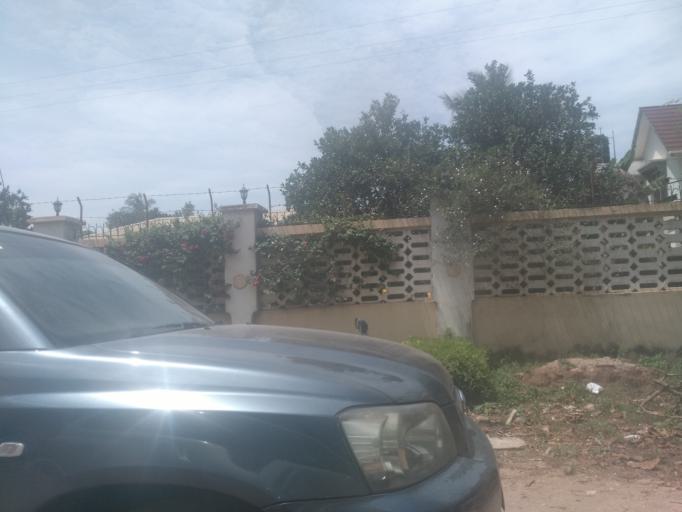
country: TZ
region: Zanzibar Urban/West
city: Zanzibar
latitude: -6.2081
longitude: 39.2104
